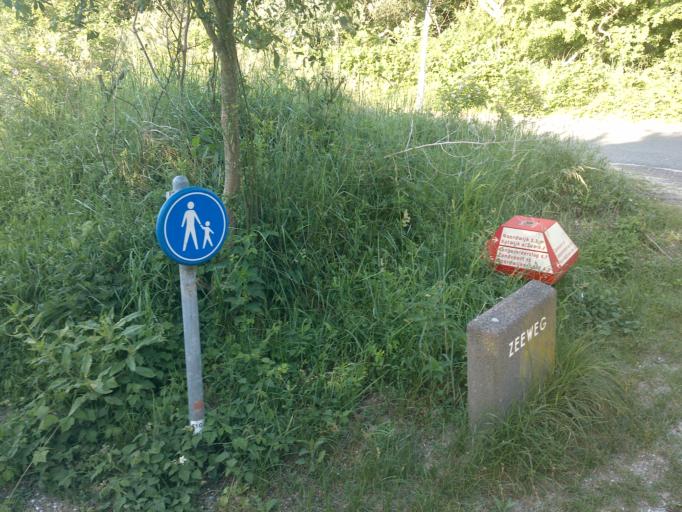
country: NL
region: South Holland
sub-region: Gemeente Noordwijk
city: Noordwijk-Binnen
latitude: 52.2579
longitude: 4.4514
